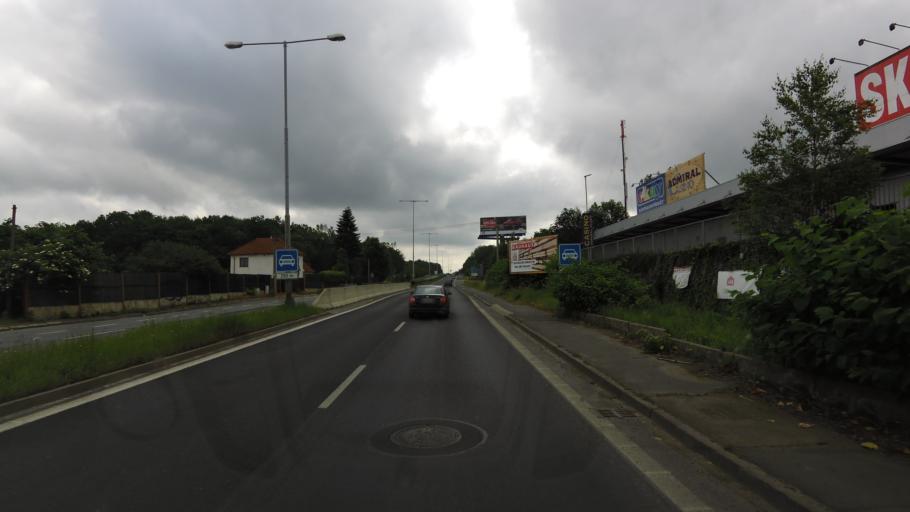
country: CZ
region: Plzensky
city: Dysina
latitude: 49.7466
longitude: 13.4429
